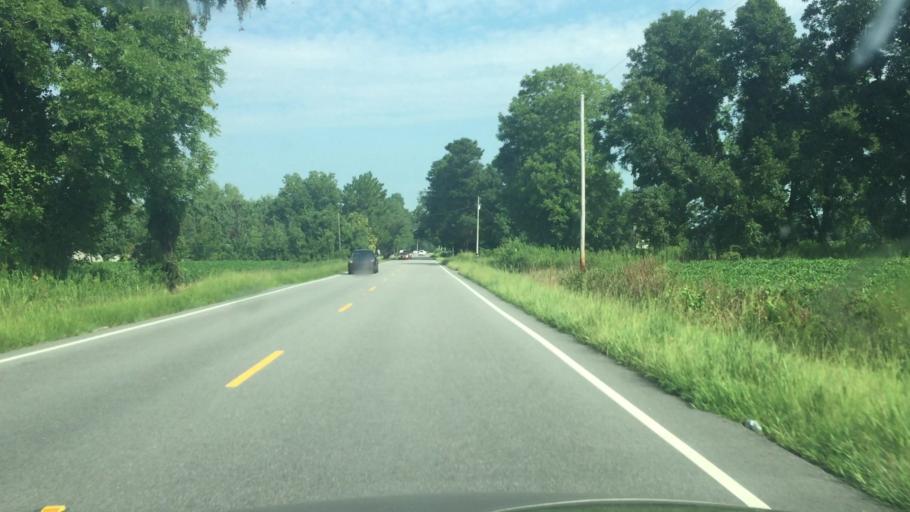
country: US
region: North Carolina
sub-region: Columbus County
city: Chadbourn
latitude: 34.2873
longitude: -78.8221
